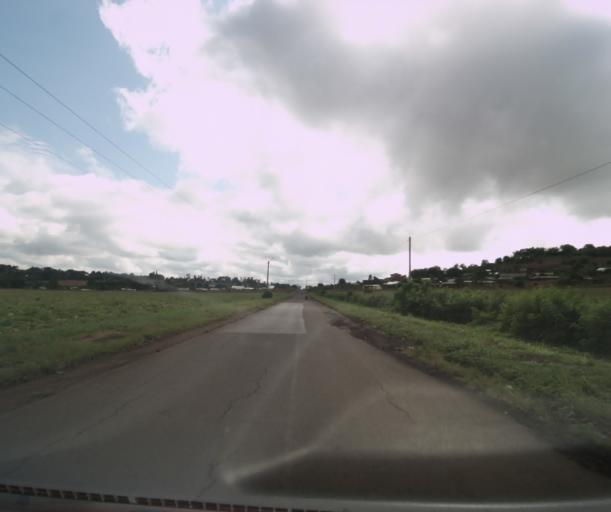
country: CM
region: West
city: Foumbot
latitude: 5.4992
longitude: 10.6155
